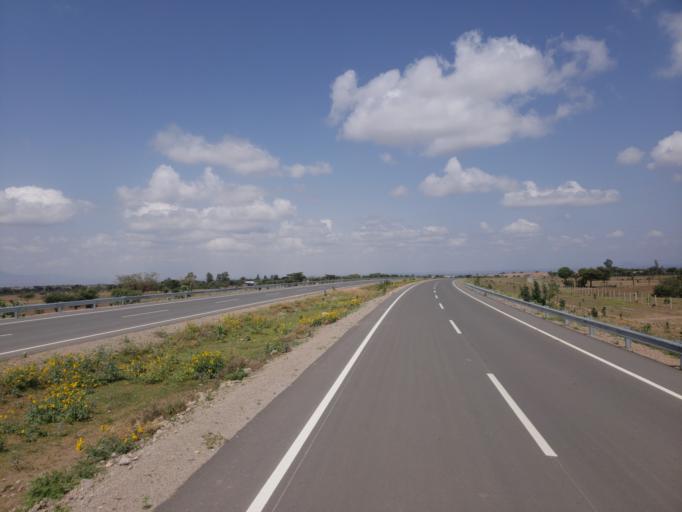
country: ET
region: Oromiya
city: Mojo
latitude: 8.5113
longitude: 39.0841
